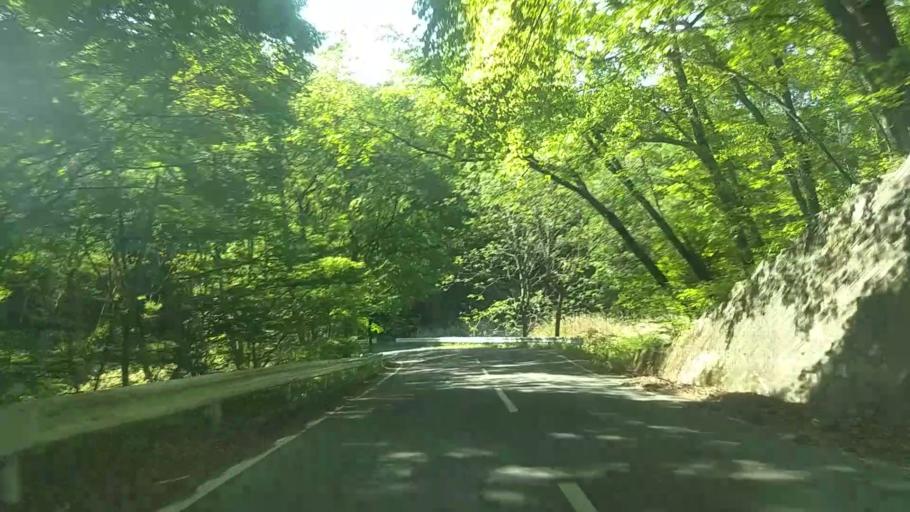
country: JP
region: Yamanashi
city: Nirasaki
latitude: 35.8837
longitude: 138.3764
